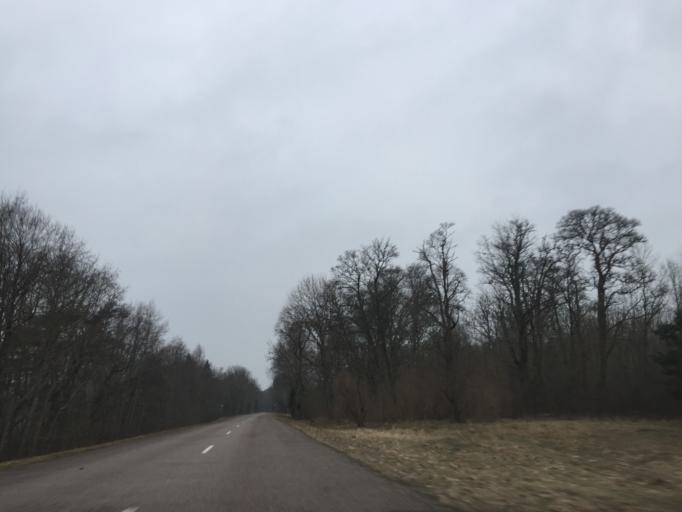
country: EE
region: Saare
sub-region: Kuressaare linn
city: Kuressaare
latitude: 58.3885
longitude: 22.2183
